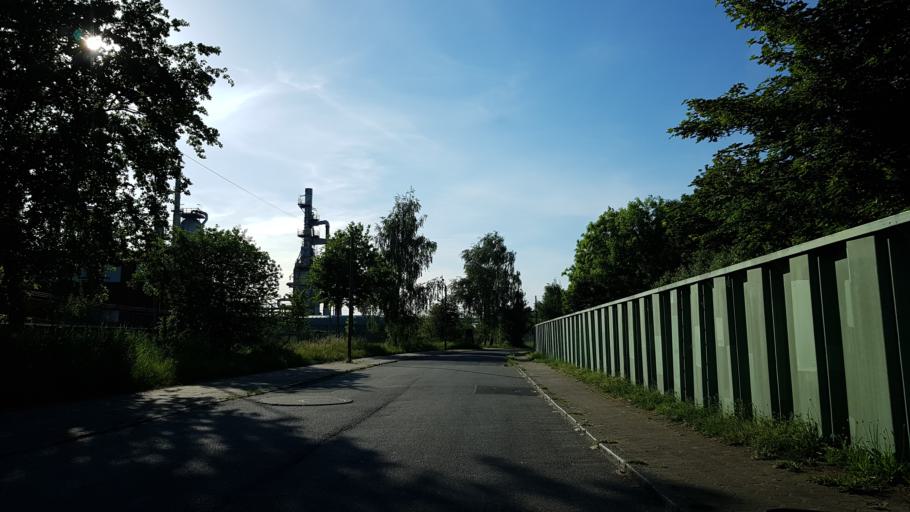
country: DE
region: Hamburg
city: Harburg
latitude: 53.4829
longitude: 9.9554
